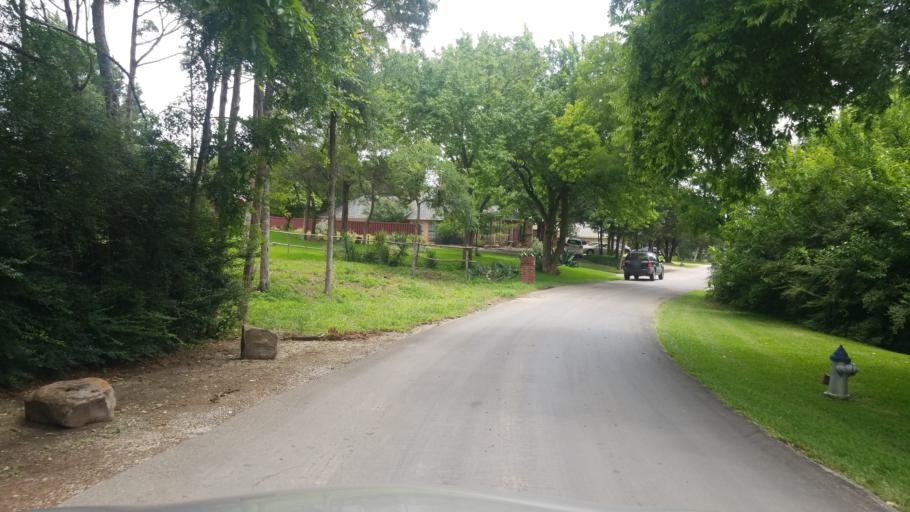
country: US
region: Texas
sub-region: Dallas County
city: Duncanville
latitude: 32.6820
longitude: -96.9326
